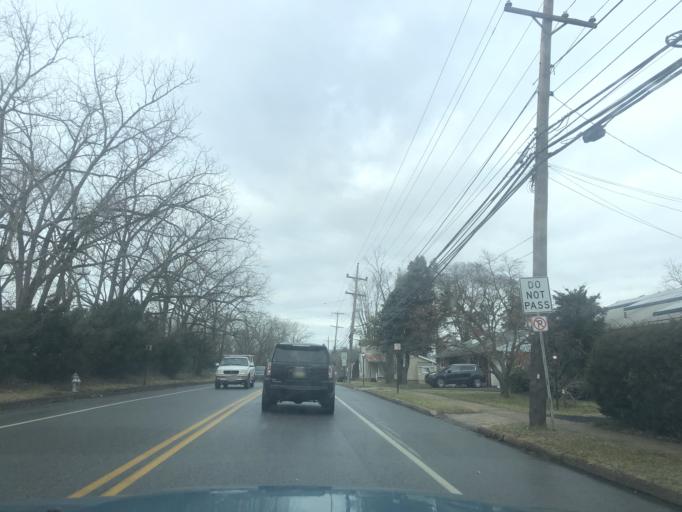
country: US
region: Pennsylvania
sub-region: Montgomery County
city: Glenside
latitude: 40.1265
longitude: -75.1428
